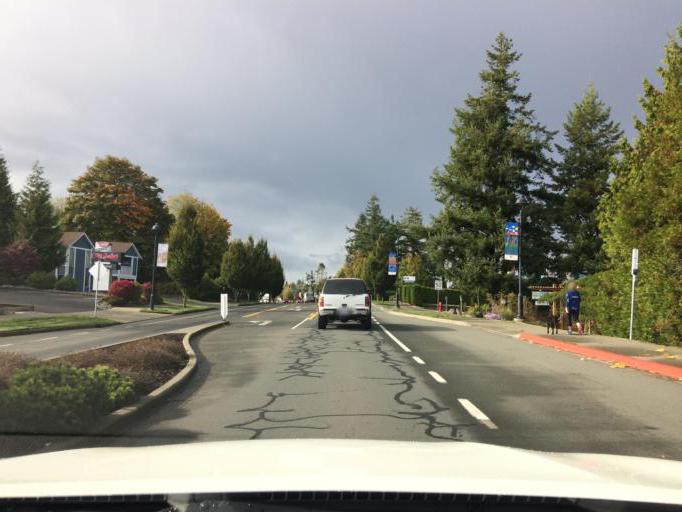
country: CA
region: British Columbia
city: Campbell River
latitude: 49.9695
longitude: -125.2119
